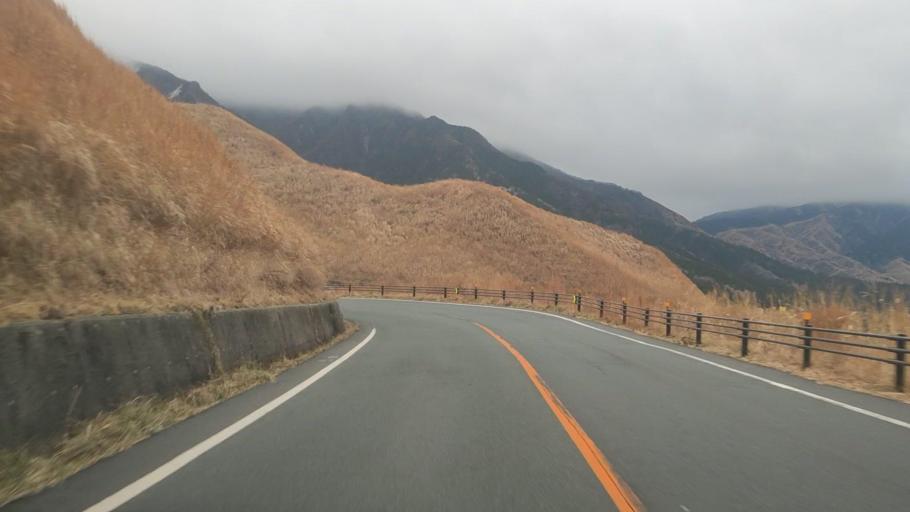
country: JP
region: Kumamoto
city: Aso
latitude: 32.9063
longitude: 131.1542
